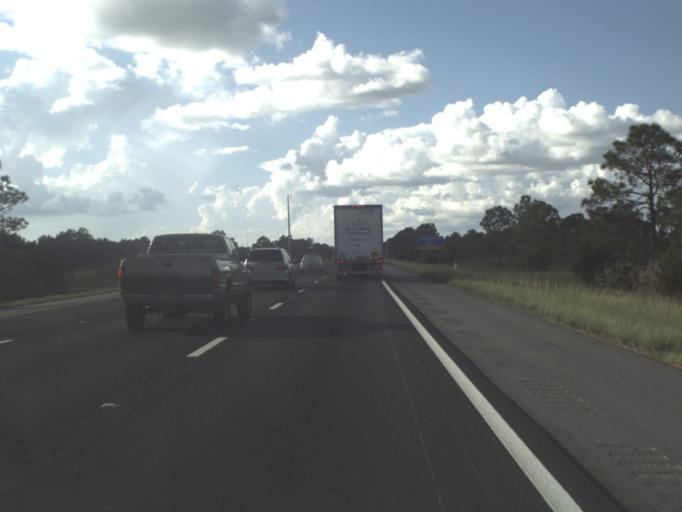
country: US
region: Florida
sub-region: Lee County
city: Burnt Store Marina
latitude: 26.8335
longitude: -81.9575
